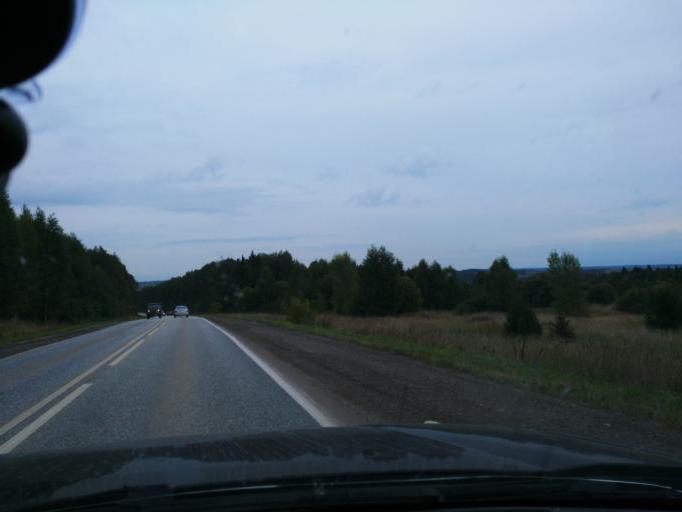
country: RU
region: Perm
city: Chernushka
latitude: 56.5904
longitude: 56.1534
